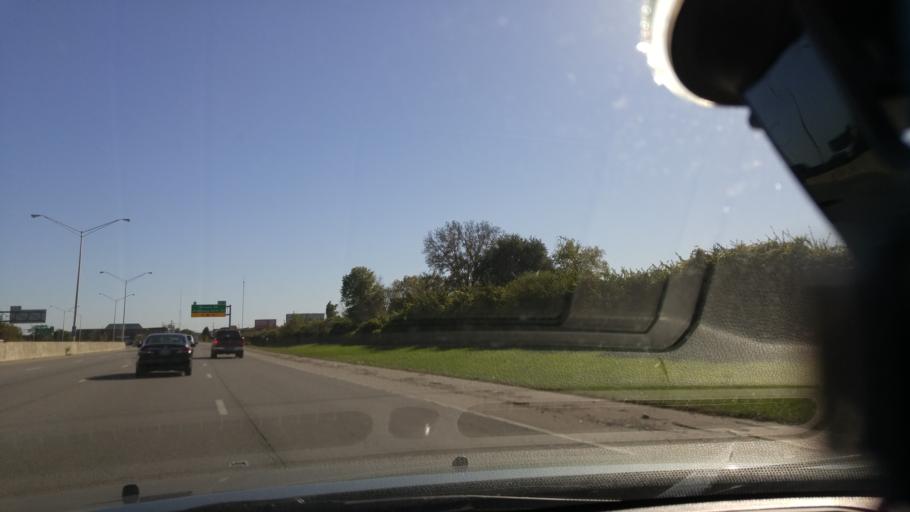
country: US
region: Ohio
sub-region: Franklin County
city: Grandview Heights
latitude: 40.0028
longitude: -83.0306
